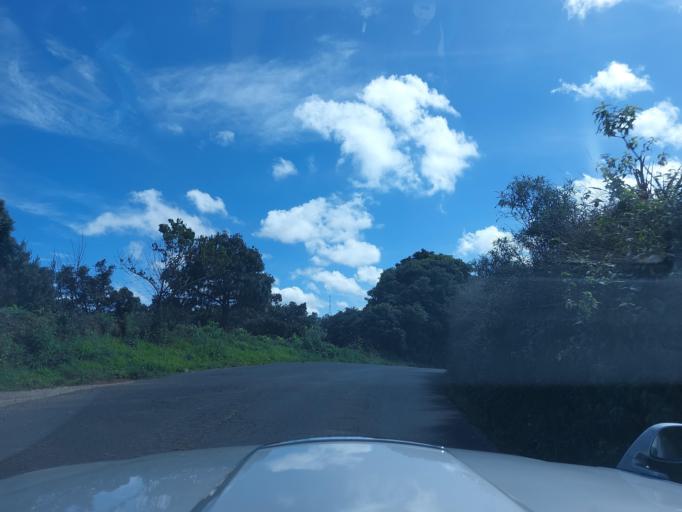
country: GT
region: Chimaltenango
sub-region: Municipio de Santa Cruz Balanya
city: Santa Cruz Balanya
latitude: 14.7098
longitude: -90.8952
